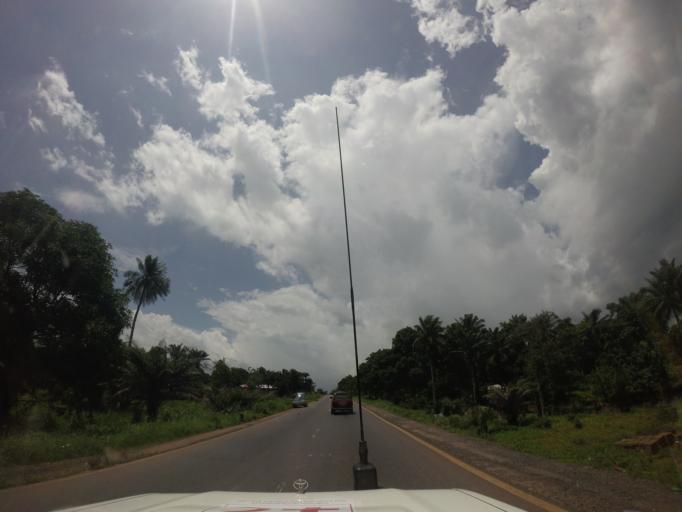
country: SL
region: Western Area
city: Waterloo
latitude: 8.3349
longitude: -13.0125
